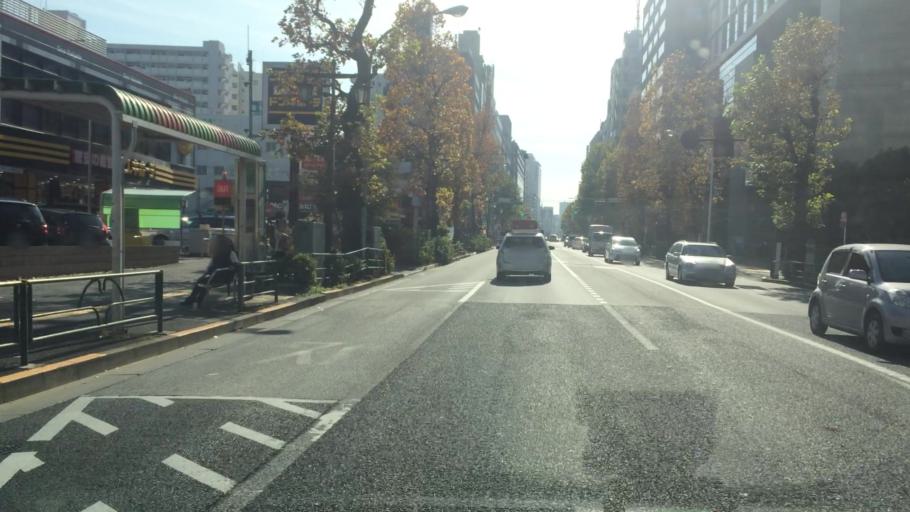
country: JP
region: Tokyo
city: Tokyo
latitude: 35.7058
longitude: 139.7088
